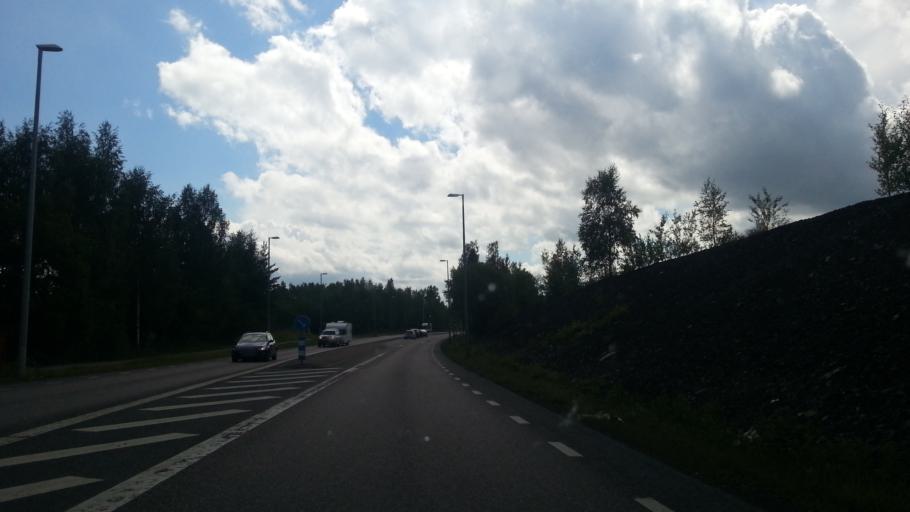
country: SE
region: Dalarna
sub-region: Faluns Kommun
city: Falun
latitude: 60.6086
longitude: 15.6171
